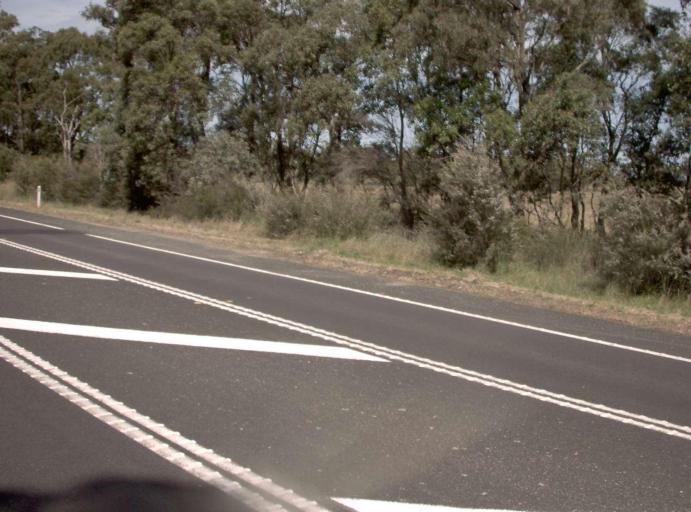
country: AU
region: Victoria
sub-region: Wellington
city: Sale
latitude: -37.9303
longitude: 147.1989
